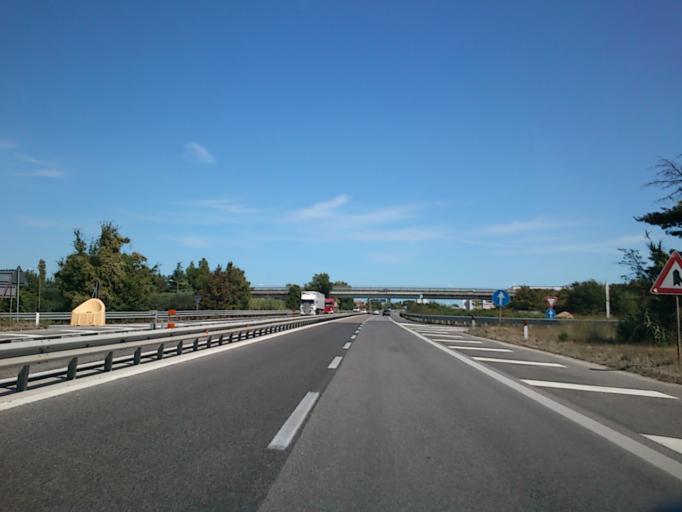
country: IT
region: The Marches
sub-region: Provincia di Pesaro e Urbino
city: Bellocchi
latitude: 43.7877
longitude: 12.9950
